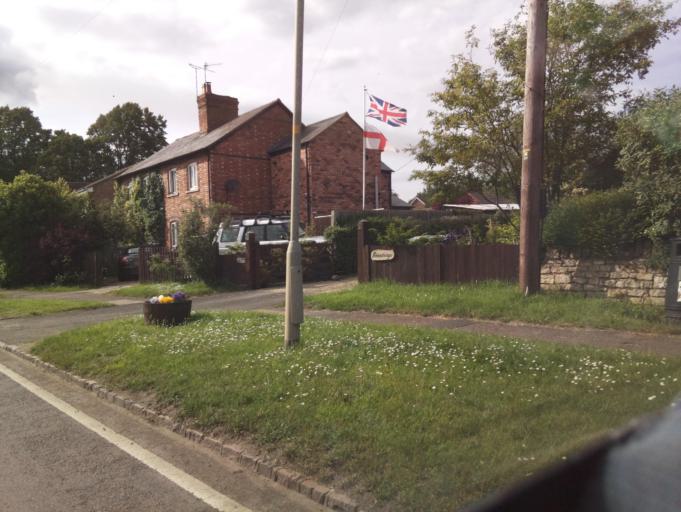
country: GB
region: England
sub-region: Worcestershire
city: South Littleton
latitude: 52.0949
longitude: -1.8712
